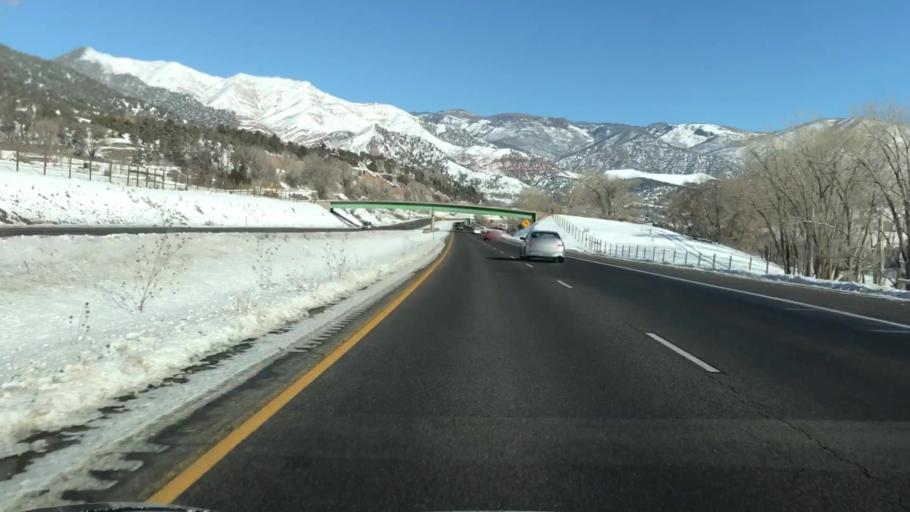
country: US
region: Colorado
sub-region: Garfield County
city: New Castle
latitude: 39.5671
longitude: -107.4879
